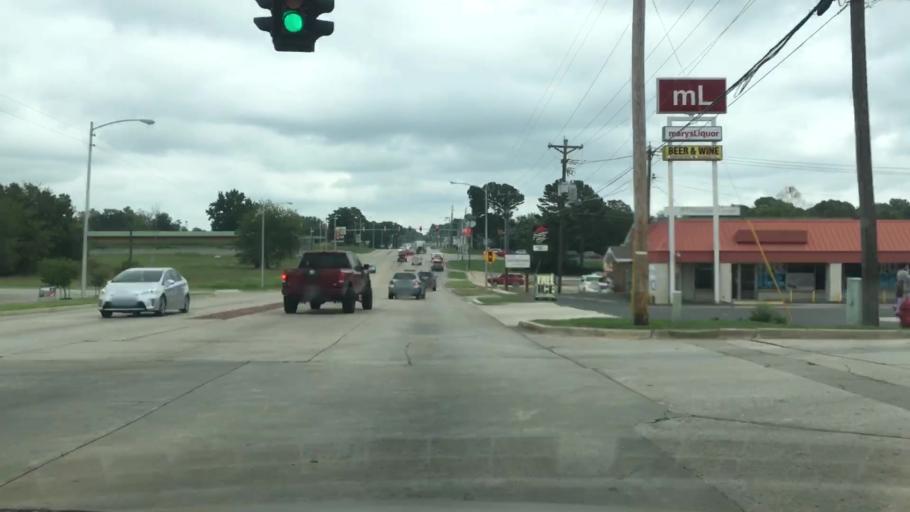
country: US
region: Oklahoma
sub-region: Cherokee County
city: Tahlequah
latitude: 35.9156
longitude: -94.9580
